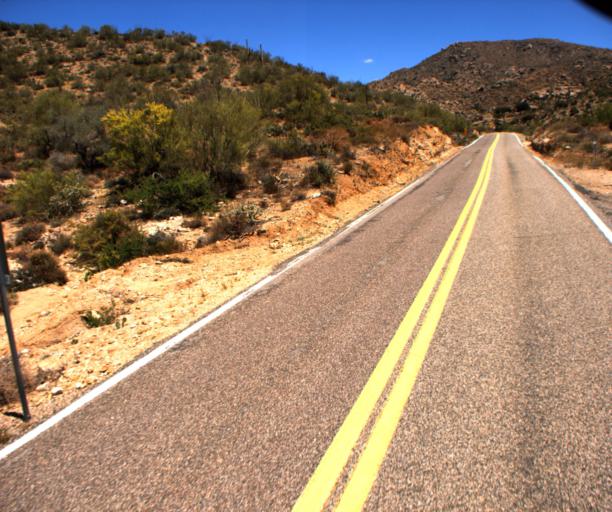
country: US
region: Arizona
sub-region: Yavapai County
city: Bagdad
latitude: 34.4533
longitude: -112.9842
